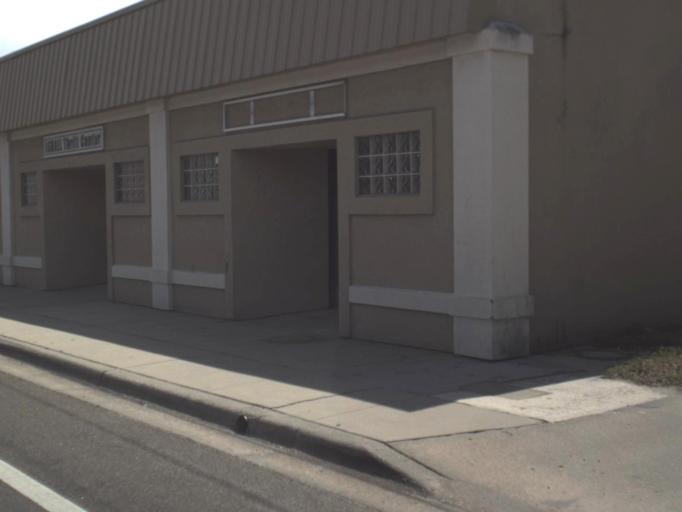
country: US
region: Florida
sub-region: Duval County
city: Jacksonville
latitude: 30.3822
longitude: -81.6498
